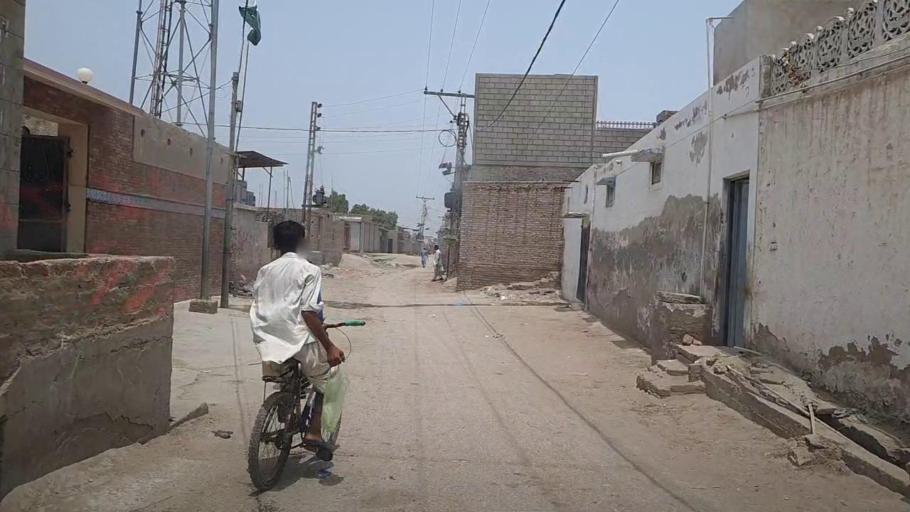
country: PK
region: Sindh
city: Sita Road
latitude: 27.0400
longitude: 67.8460
